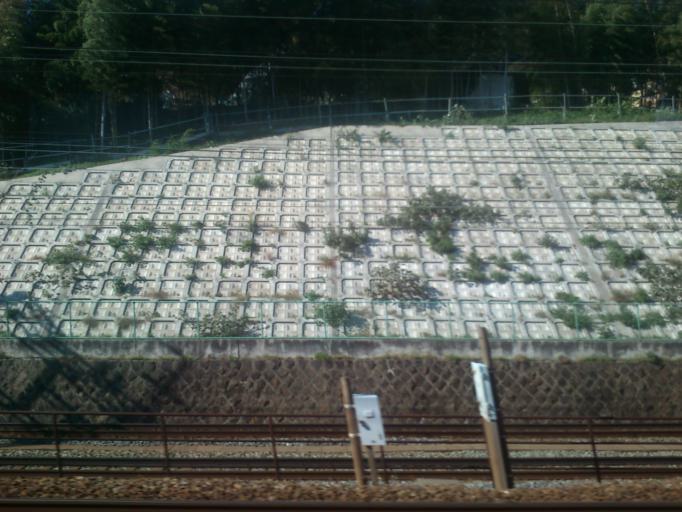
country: JP
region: Kyoto
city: Yawata
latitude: 34.8989
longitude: 135.6847
